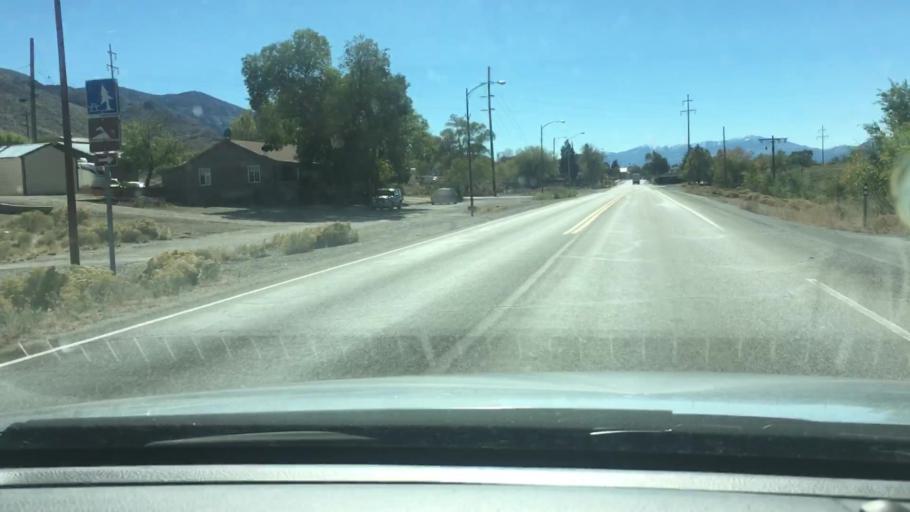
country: US
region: Nevada
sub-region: White Pine County
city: McGill
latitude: 39.4116
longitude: -114.7757
